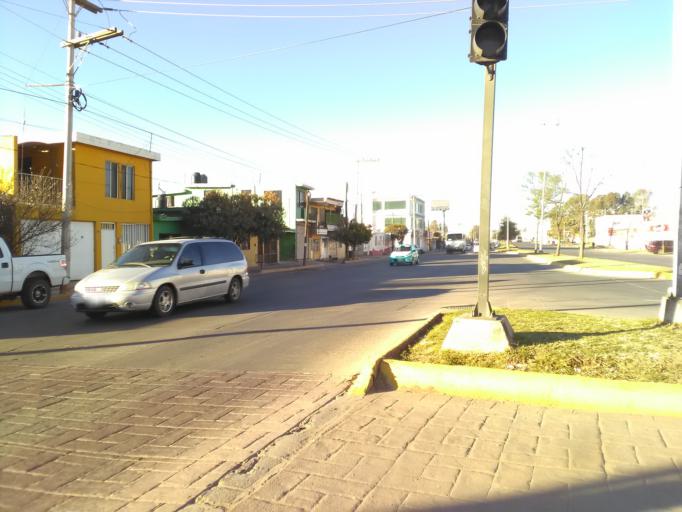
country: MX
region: Durango
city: Victoria de Durango
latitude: 24.0474
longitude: -104.6514
